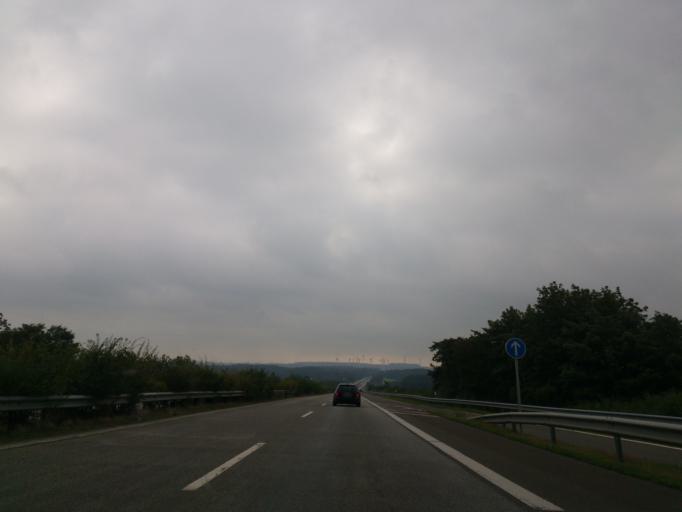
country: DE
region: Schleswig-Holstein
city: Schafstedt
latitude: 54.0685
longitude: 9.3226
